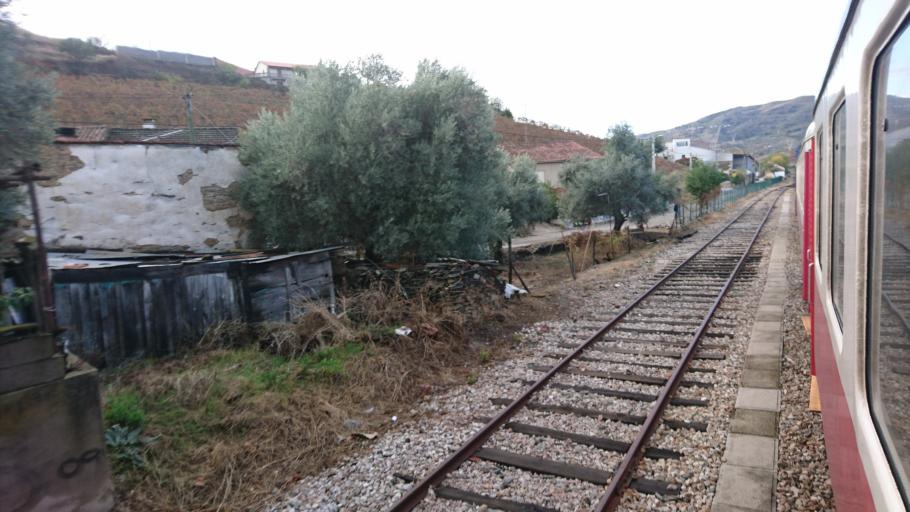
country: PT
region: Braganca
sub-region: Torre de Moncorvo
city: Torre de Moncorvo
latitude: 41.1294
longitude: -7.1256
